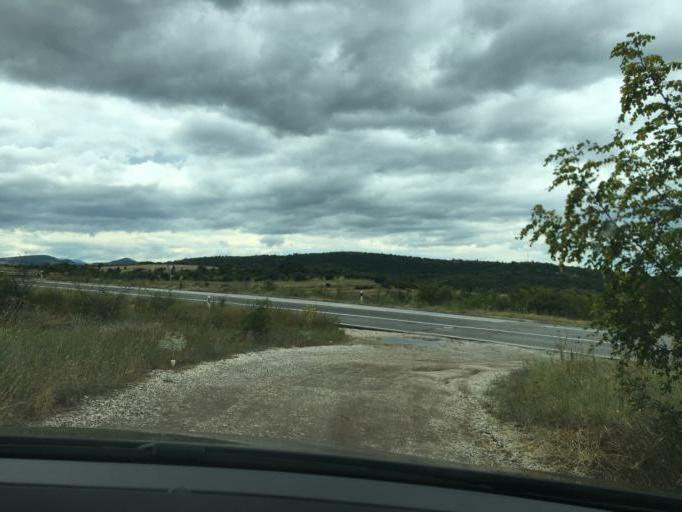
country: MK
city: Klechovce
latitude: 42.1565
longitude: 21.9385
